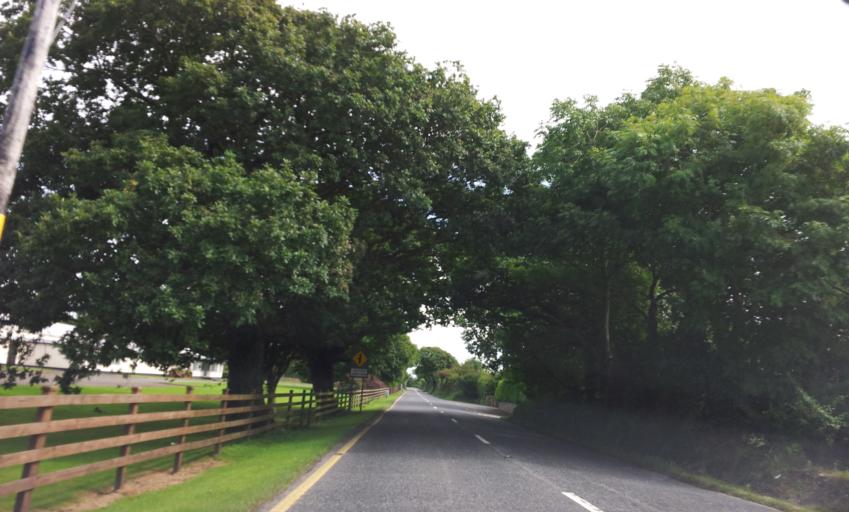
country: IE
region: Munster
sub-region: Ciarrai
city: Killorglin
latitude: 52.1002
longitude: -9.7538
